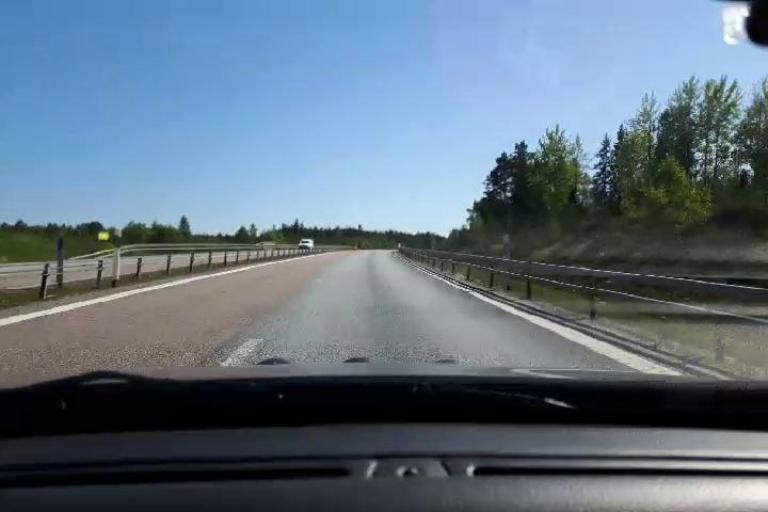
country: SE
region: Gaevleborg
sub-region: Soderhamns Kommun
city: Soderhamn
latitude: 61.3459
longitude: 17.0194
